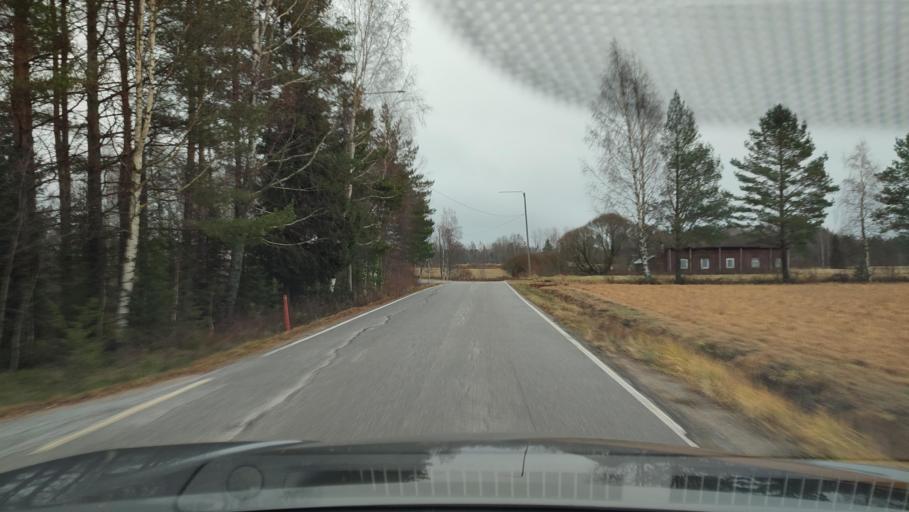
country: FI
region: Southern Ostrobothnia
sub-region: Suupohja
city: Isojoki
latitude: 62.1809
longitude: 21.9130
